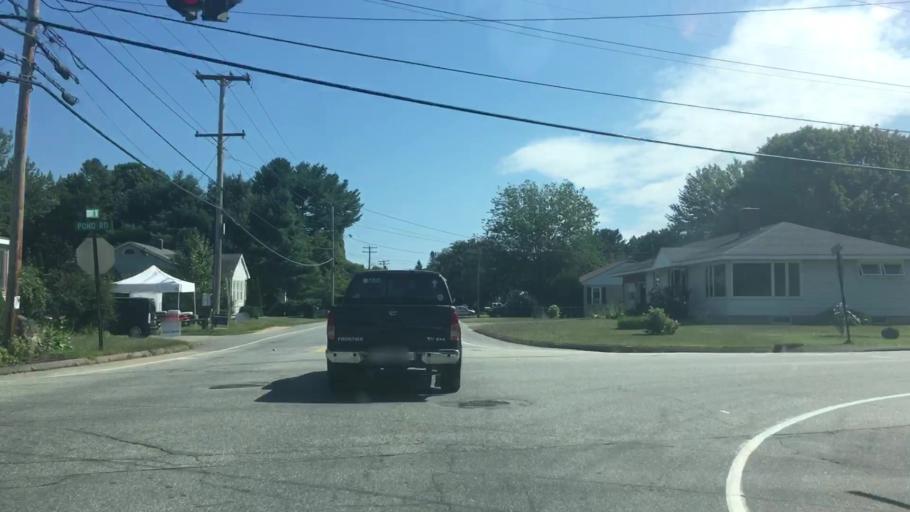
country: US
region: Maine
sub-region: Androscoggin County
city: Sabattus
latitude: 44.0973
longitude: -70.1569
